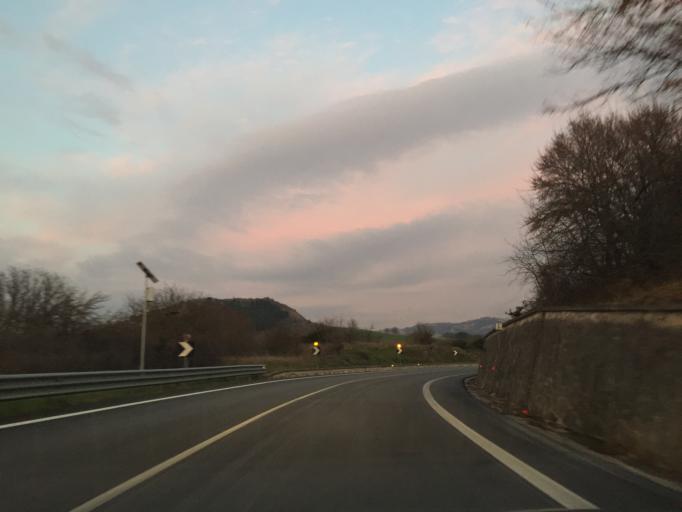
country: IT
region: Molise
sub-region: Provincia di Campobasso
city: Gambatesa
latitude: 41.5251
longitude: 14.9334
